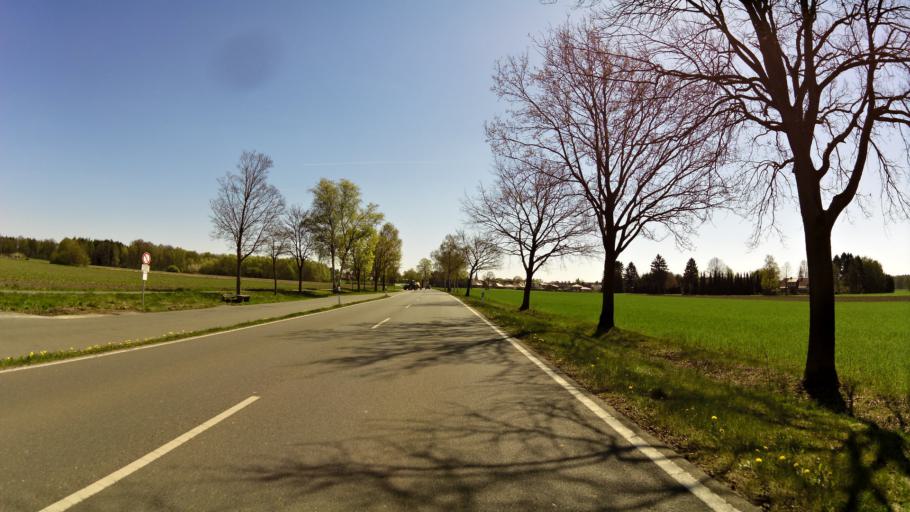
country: DE
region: Lower Saxony
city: Soltau
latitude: 52.9981
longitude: 9.8173
